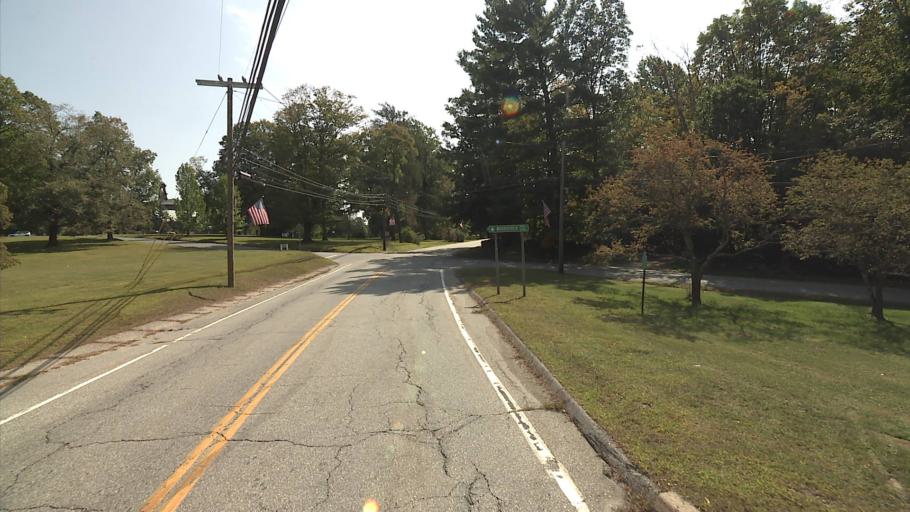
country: US
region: Connecticut
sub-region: Windham County
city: South Woodstock
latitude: 41.9509
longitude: -71.9778
